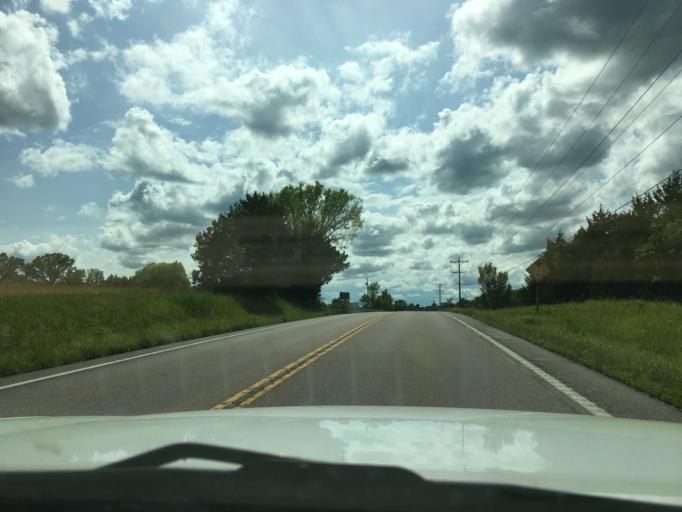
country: US
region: Missouri
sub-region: Franklin County
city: Gerald
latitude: 38.3874
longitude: -91.3884
